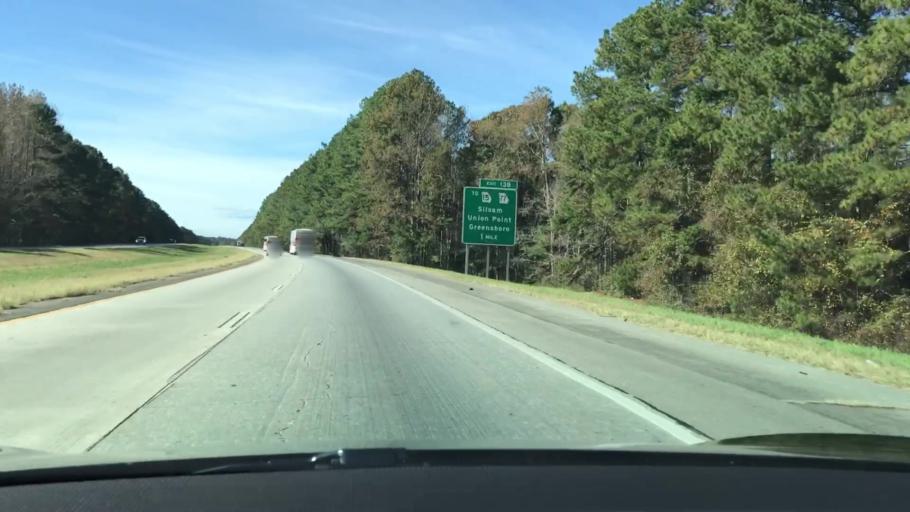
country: US
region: Georgia
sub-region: Greene County
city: Union Point
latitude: 33.5499
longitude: -83.0580
